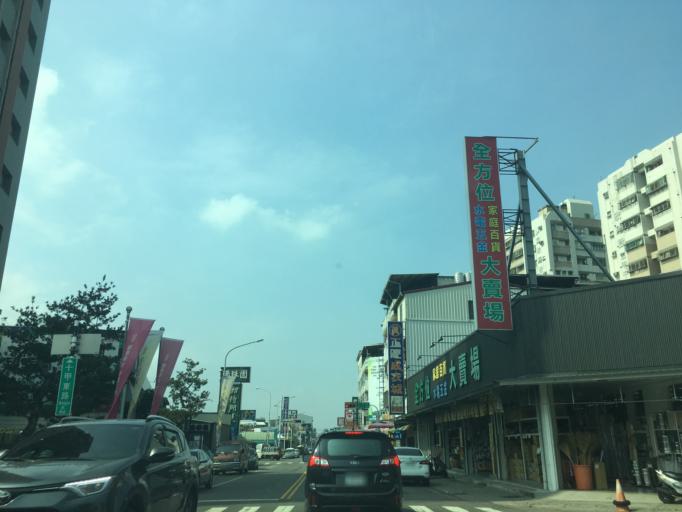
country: TW
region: Taiwan
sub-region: Taichung City
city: Taichung
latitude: 24.1451
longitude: 120.7094
